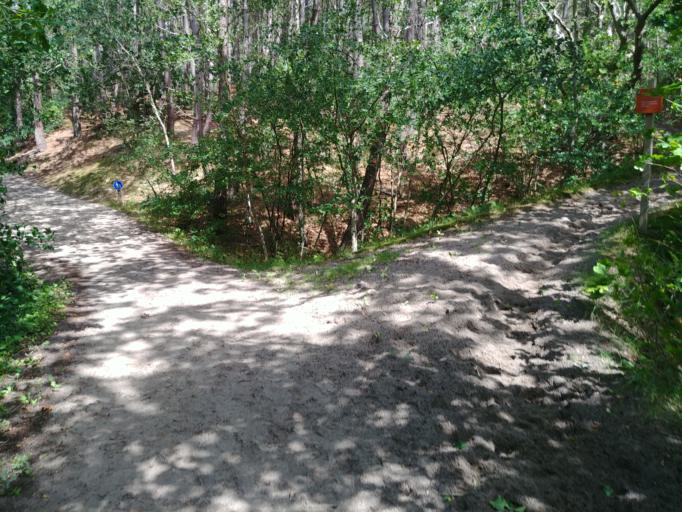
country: NL
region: North Holland
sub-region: Gemeente Alkmaar
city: Alkmaar
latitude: 52.6819
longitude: 4.6920
